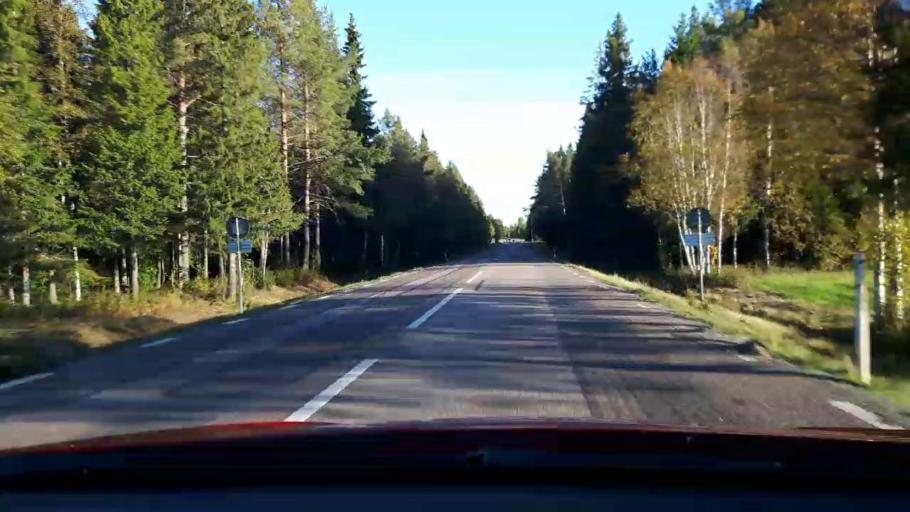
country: SE
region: Jaemtland
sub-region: OEstersunds Kommun
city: Brunflo
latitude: 63.0523
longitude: 14.8603
